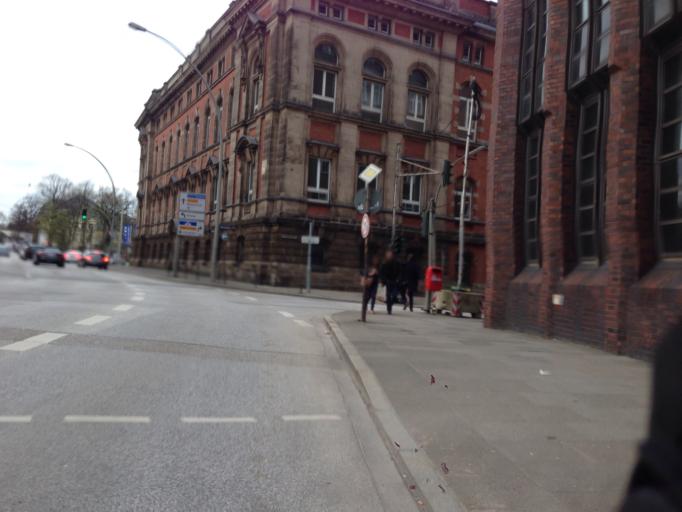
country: DE
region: Hamburg
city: Neustadt
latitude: 53.5567
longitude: 9.9843
